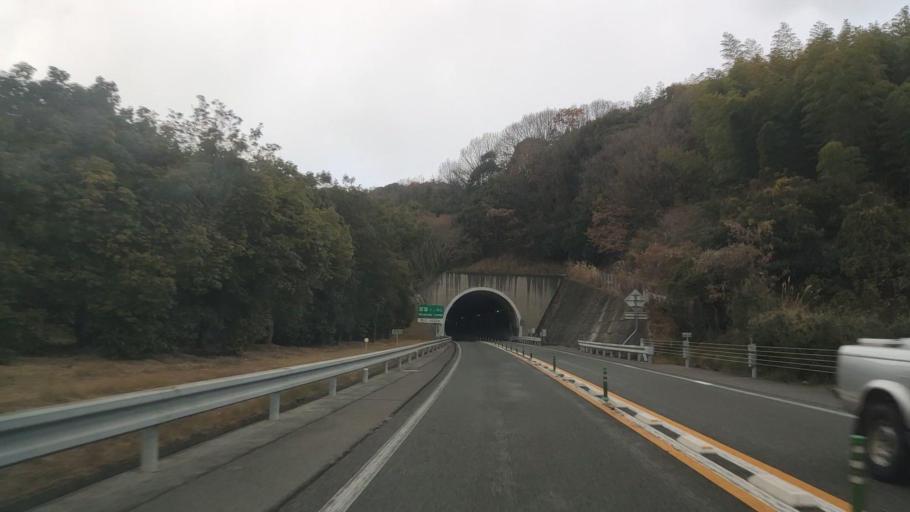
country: JP
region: Hiroshima
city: Innoshima
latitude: 34.1748
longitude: 133.0678
